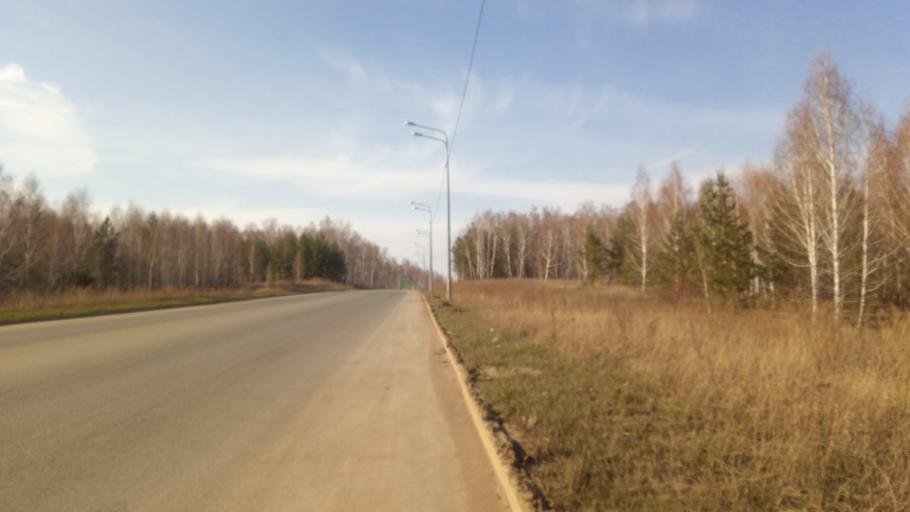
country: RU
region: Chelyabinsk
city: Sargazy
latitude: 55.1179
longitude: 61.2535
